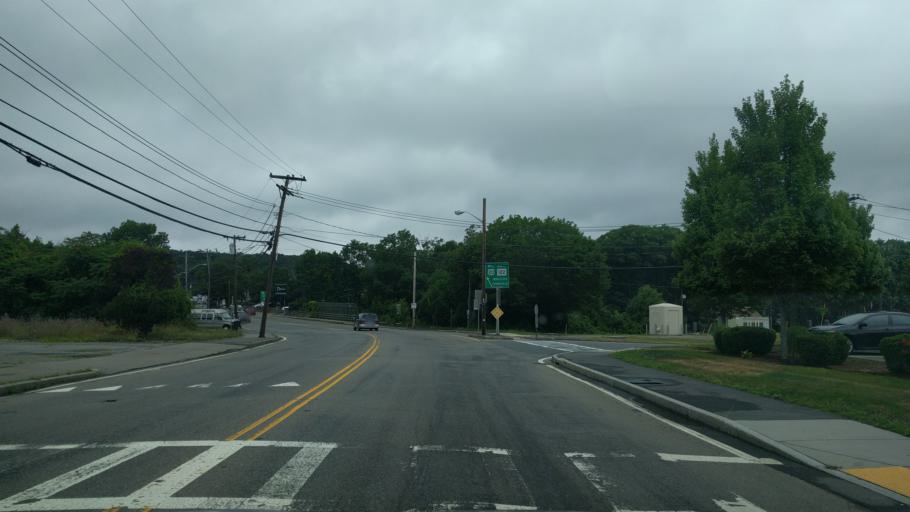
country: US
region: Massachusetts
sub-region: Worcester County
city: Sunderland
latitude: 42.2347
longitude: -71.7477
